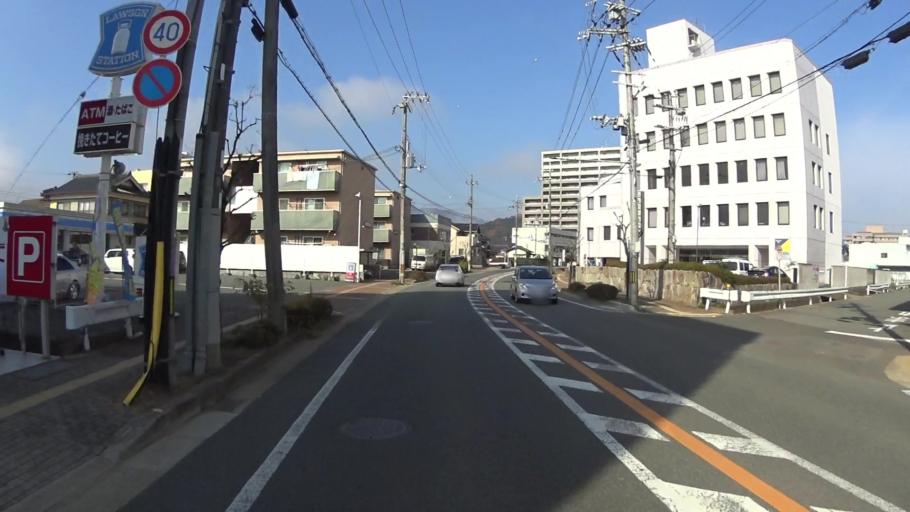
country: JP
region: Kyoto
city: Fukuchiyama
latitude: 35.2990
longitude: 135.1131
